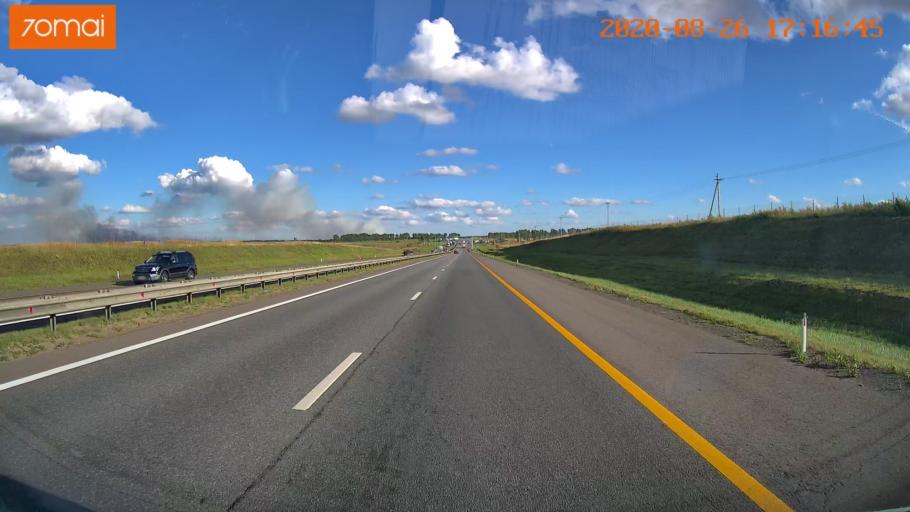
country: RU
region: Tula
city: Volovo
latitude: 53.6323
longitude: 38.0763
